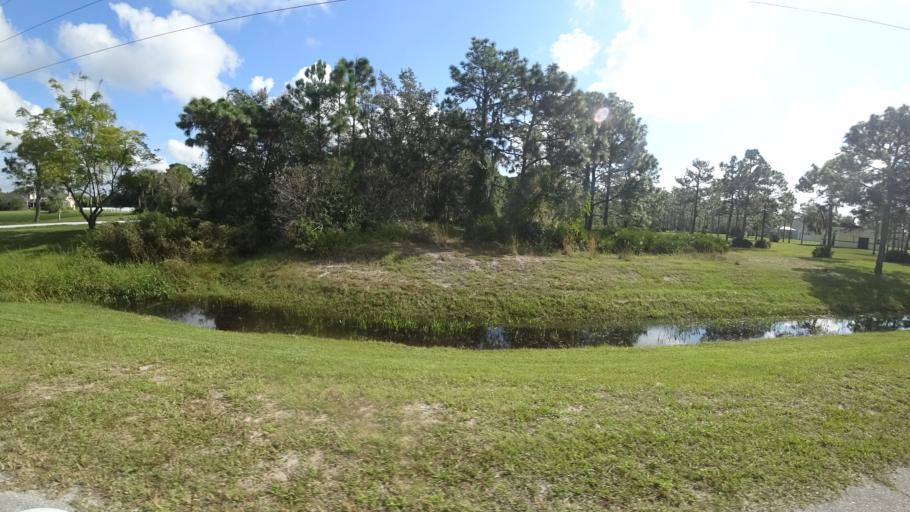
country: US
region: Florida
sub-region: Sarasota County
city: The Meadows
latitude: 27.4002
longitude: -82.3401
